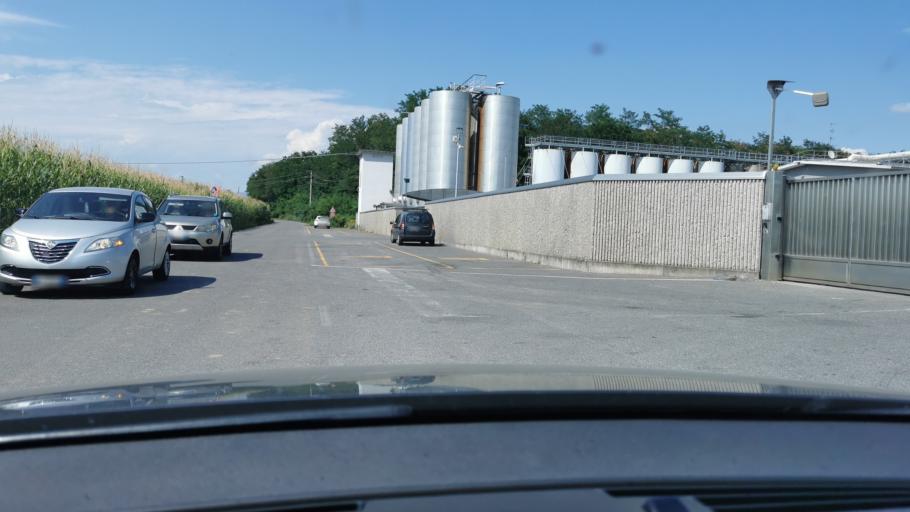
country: IT
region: Lombardy
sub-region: Provincia di Como
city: Cirimido
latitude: 45.6823
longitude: 9.0109
